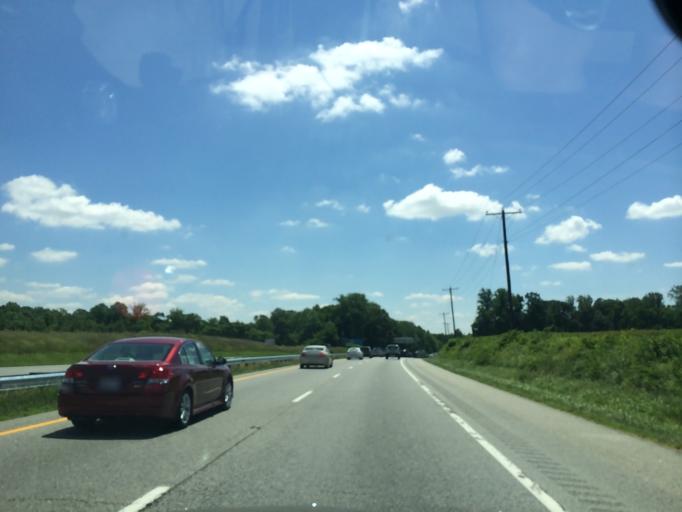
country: US
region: Maryland
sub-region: Queen Anne's County
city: Centreville
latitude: 38.9524
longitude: -76.0714
